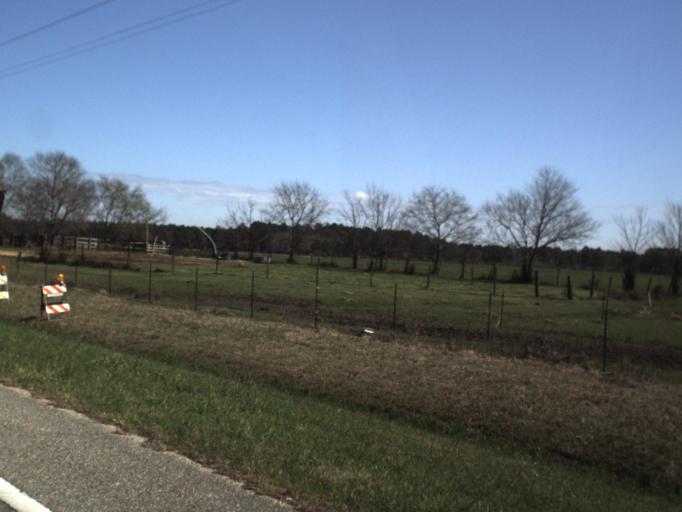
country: US
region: Florida
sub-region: Calhoun County
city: Blountstown
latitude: 30.5102
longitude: -85.0344
